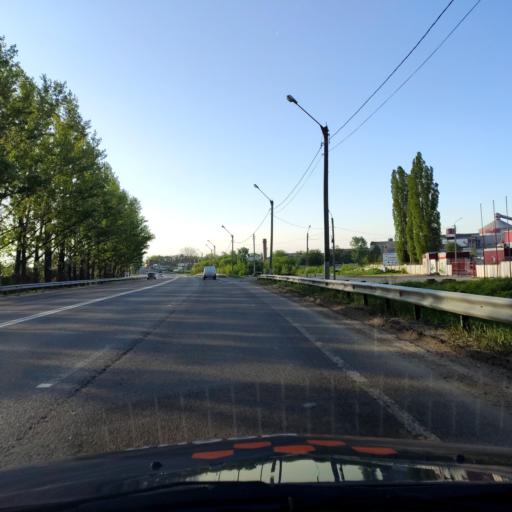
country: RU
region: Lipetsk
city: Yelets
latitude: 52.5979
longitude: 38.4755
